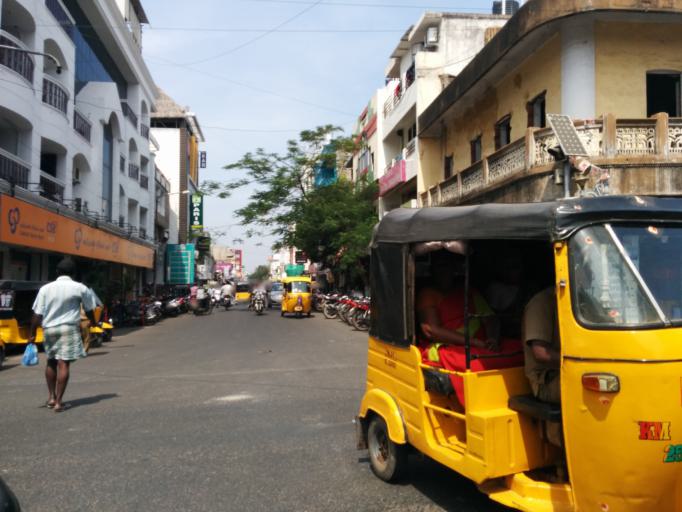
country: IN
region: Pondicherry
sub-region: Puducherry
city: Puducherry
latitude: 11.9294
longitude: 79.8281
